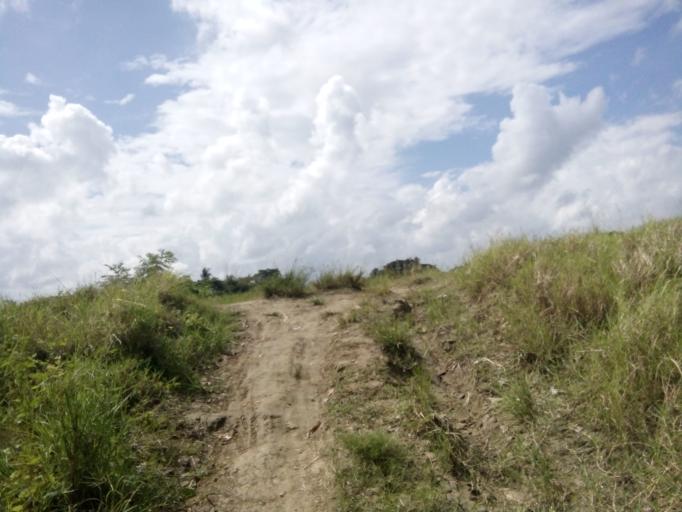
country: MM
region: Yangon
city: Kanbe
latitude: 16.8723
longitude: 95.9802
